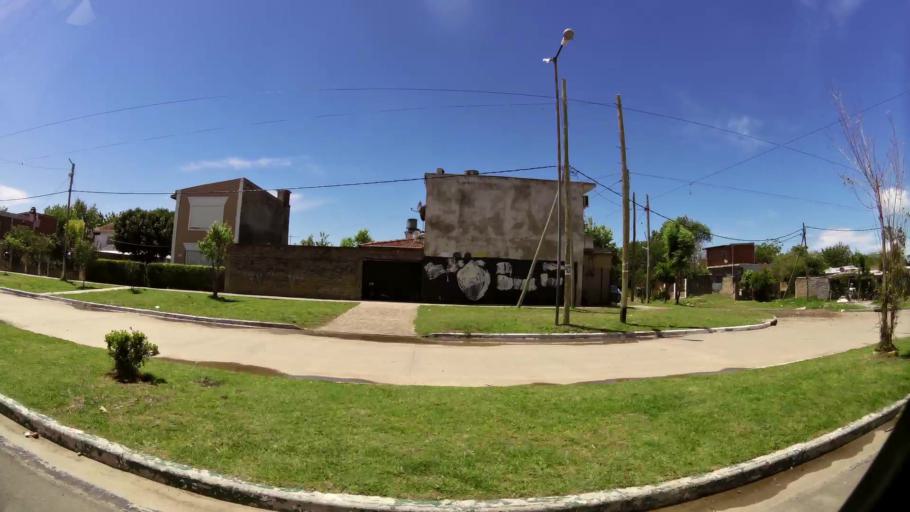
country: AR
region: Buenos Aires
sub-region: Partido de Quilmes
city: Quilmes
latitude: -34.7460
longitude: -58.3066
